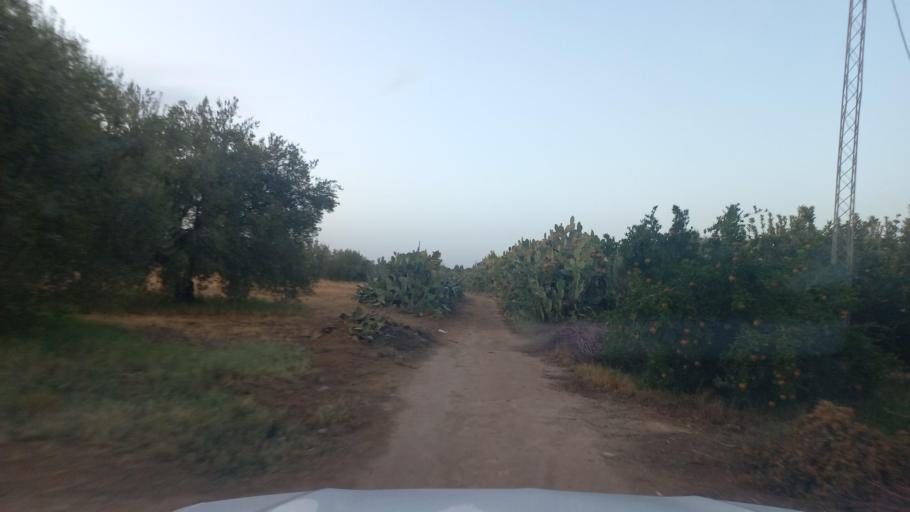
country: TN
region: Al Qasrayn
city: Kasserine
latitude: 35.2232
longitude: 9.0510
